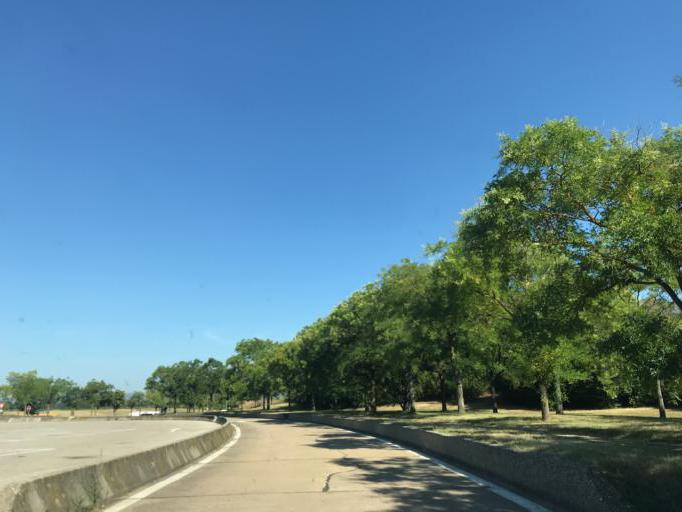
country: FR
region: Rhone-Alpes
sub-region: Departement de l'Ain
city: Civrieux
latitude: 45.8911
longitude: 4.8939
